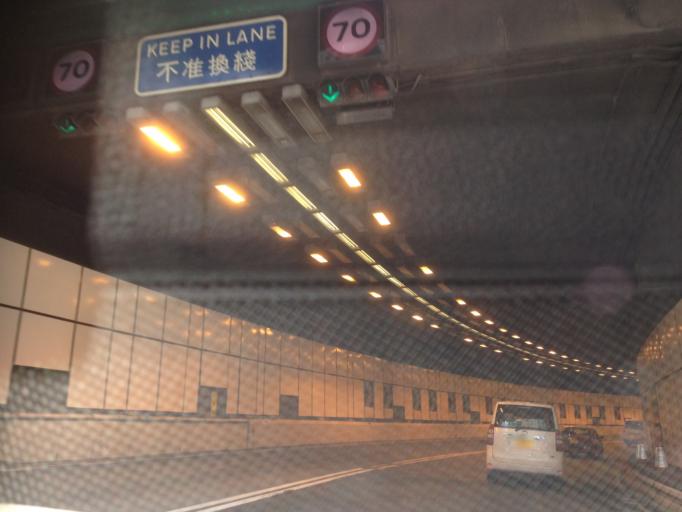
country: HK
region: Kowloon City
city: Kowloon
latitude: 22.2891
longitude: 114.2120
